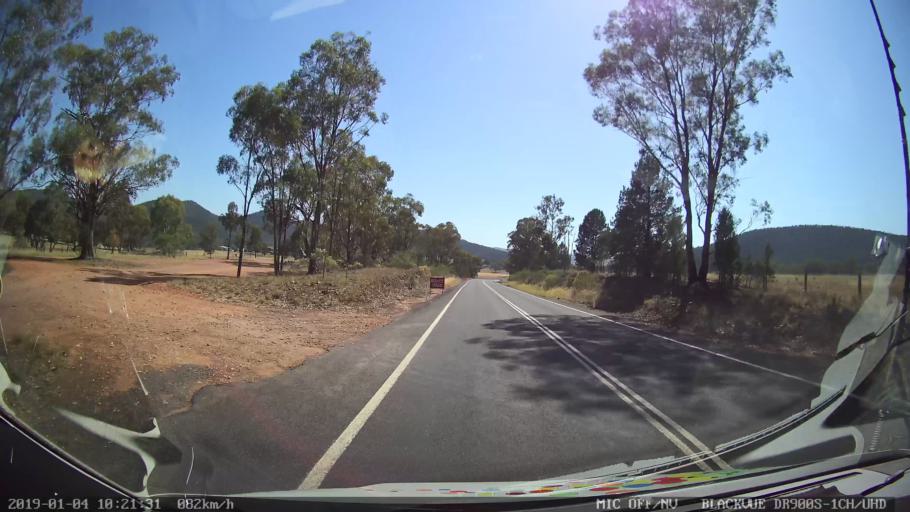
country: AU
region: New South Wales
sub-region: Cabonne
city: Canowindra
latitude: -33.3723
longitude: 148.5116
